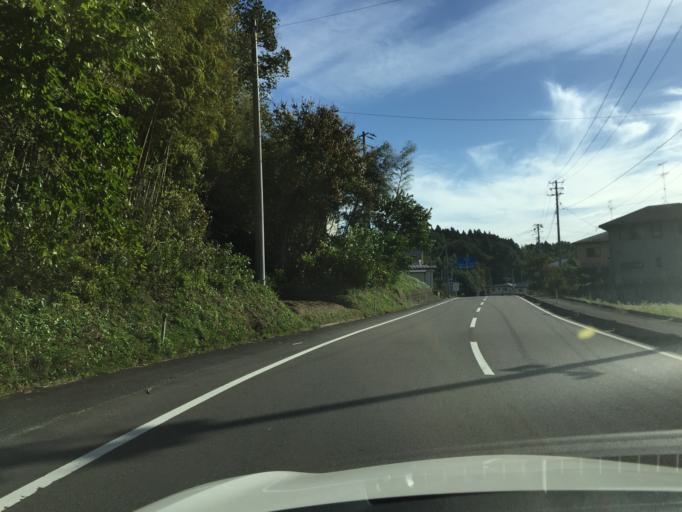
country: JP
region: Fukushima
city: Miharu
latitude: 37.4274
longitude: 140.4650
